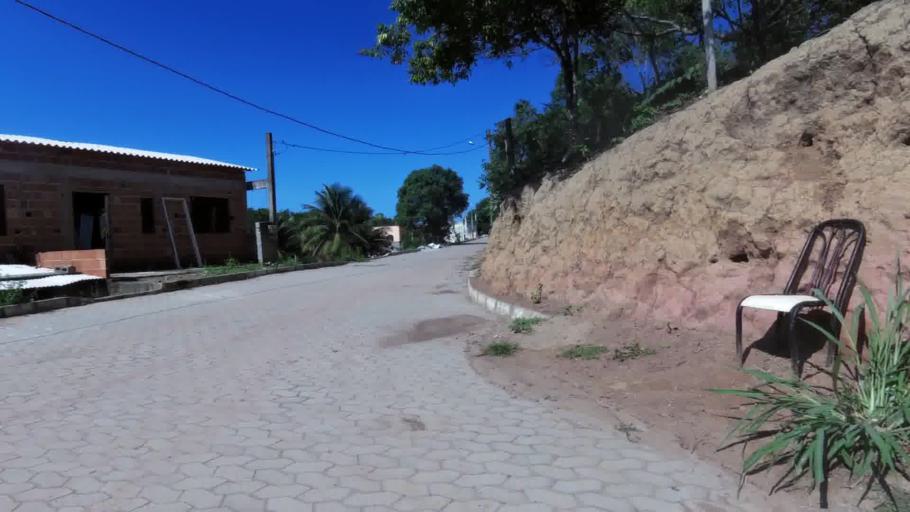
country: BR
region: Espirito Santo
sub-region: Piuma
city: Piuma
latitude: -20.8261
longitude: -40.6251
